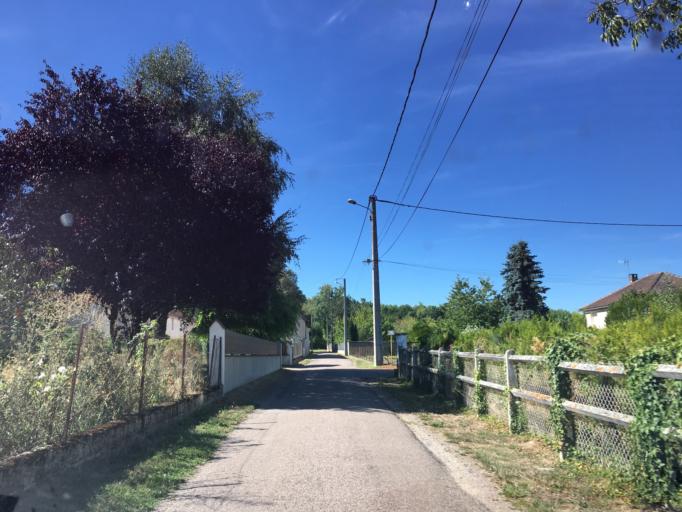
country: FR
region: Bourgogne
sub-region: Departement de l'Yonne
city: Fleury-la-Vallee
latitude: 47.8684
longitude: 3.4465
